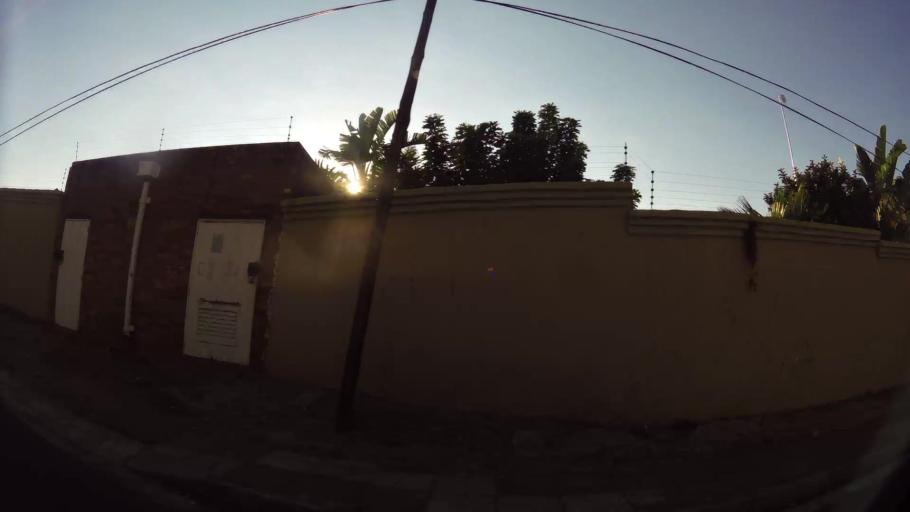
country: ZA
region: Gauteng
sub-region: Ekurhuleni Metropolitan Municipality
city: Germiston
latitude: -26.1814
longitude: 28.1560
